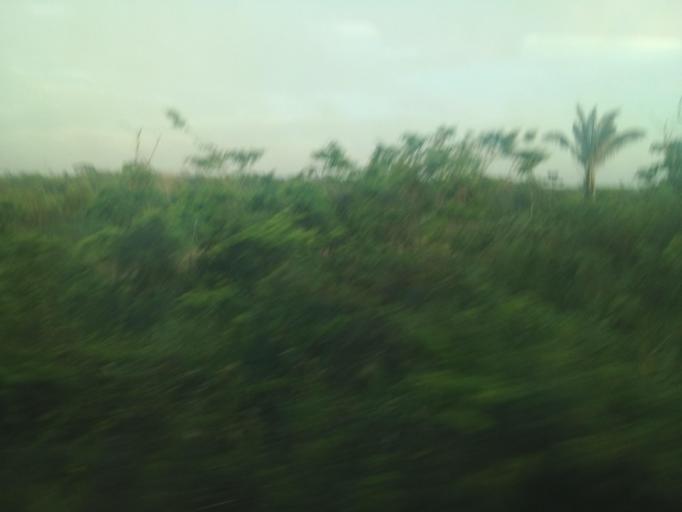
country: BR
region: Maranhao
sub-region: Imperatriz
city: Imperatriz
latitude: -4.9262
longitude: -47.4256
